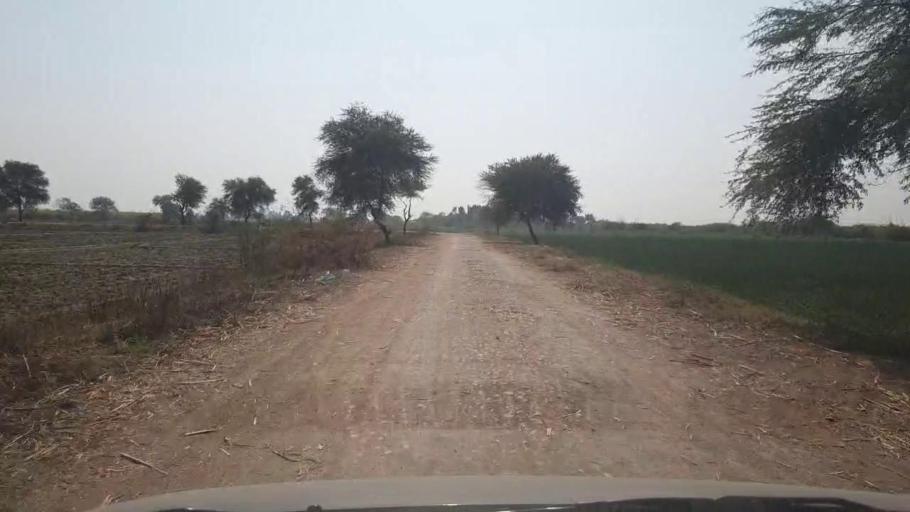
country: PK
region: Sindh
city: Mirwah Gorchani
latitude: 25.3056
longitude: 69.1575
